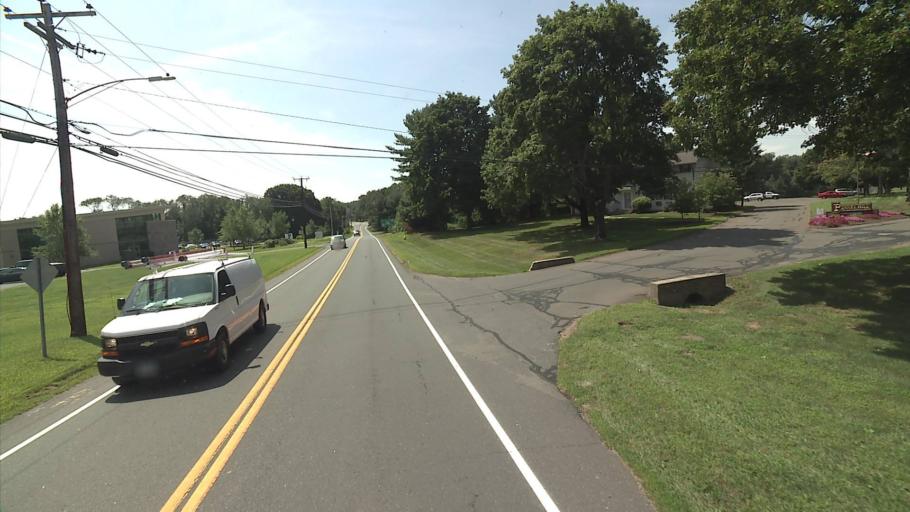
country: US
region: Connecticut
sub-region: Tolland County
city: Ellington
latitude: 41.8707
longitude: -72.4909
